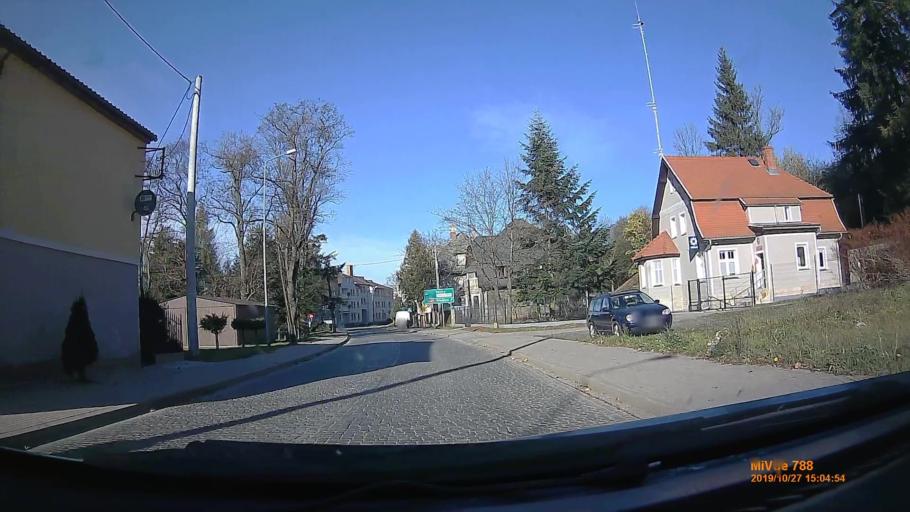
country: PL
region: Lower Silesian Voivodeship
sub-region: Powiat klodzki
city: Miedzylesie
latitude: 50.1434
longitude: 16.6634
